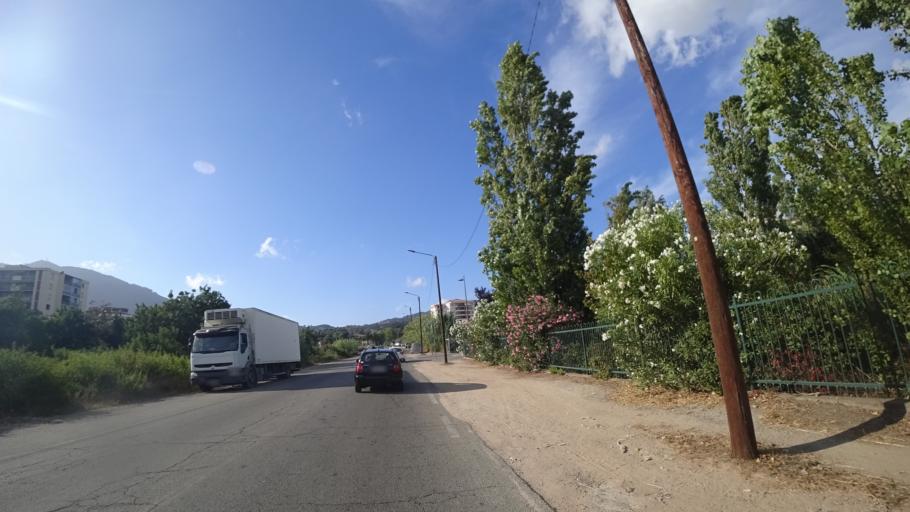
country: FR
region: Corsica
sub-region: Departement de la Corse-du-Sud
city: Ajaccio
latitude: 41.9373
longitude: 8.7426
